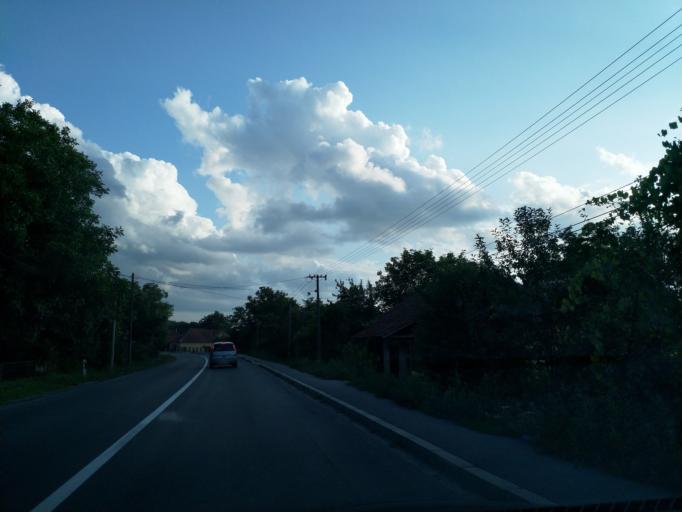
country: RS
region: Central Serbia
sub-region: Rasinski Okrug
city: Cicevac
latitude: 43.7102
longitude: 21.4368
